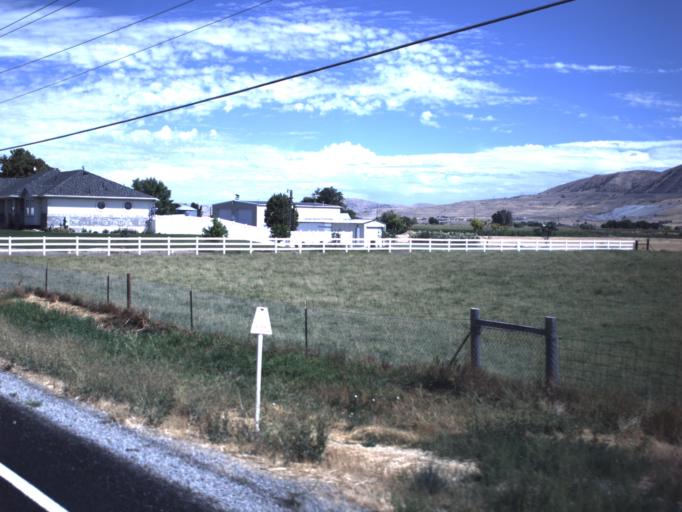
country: US
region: Utah
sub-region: Box Elder County
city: Tremonton
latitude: 41.7199
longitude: -112.1426
